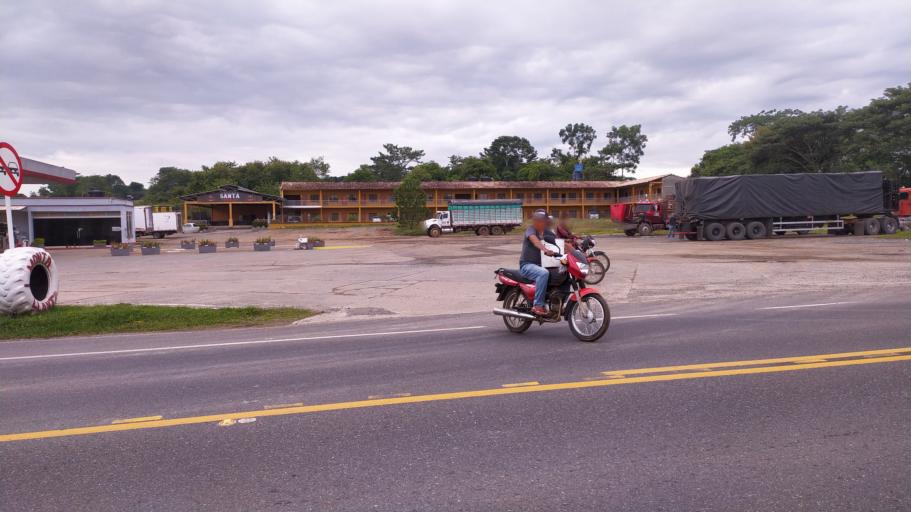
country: CO
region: Antioquia
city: Caucasia
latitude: 8.0055
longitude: -75.2407
